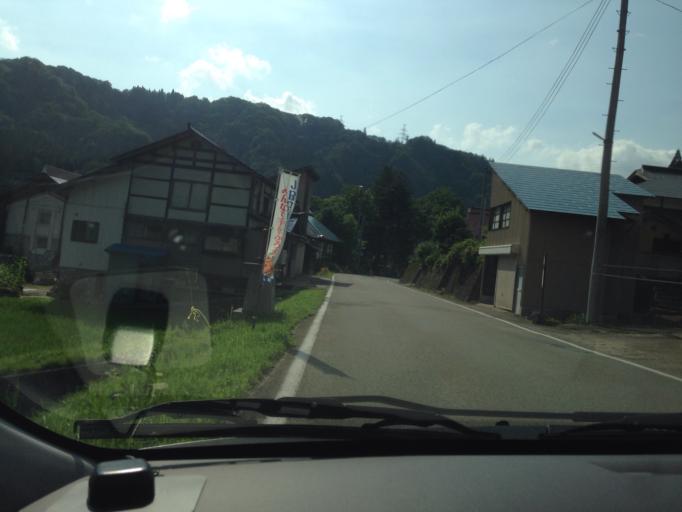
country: JP
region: Fukushima
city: Kitakata
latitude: 37.4364
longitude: 139.5306
